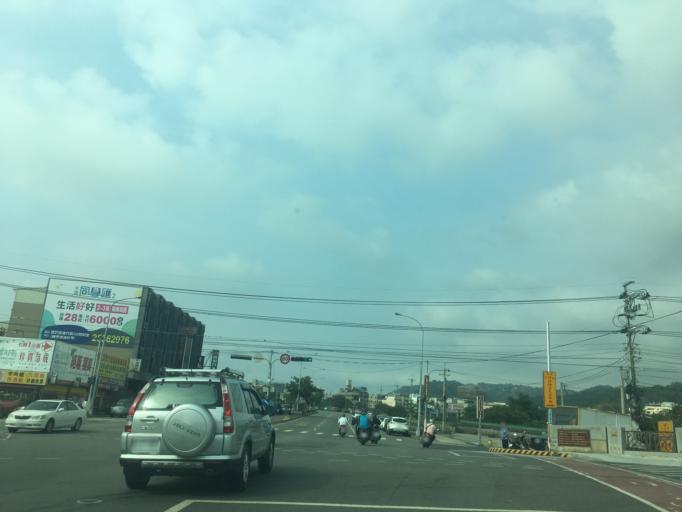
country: TW
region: Taiwan
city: Fengyuan
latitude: 24.2433
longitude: 120.7297
